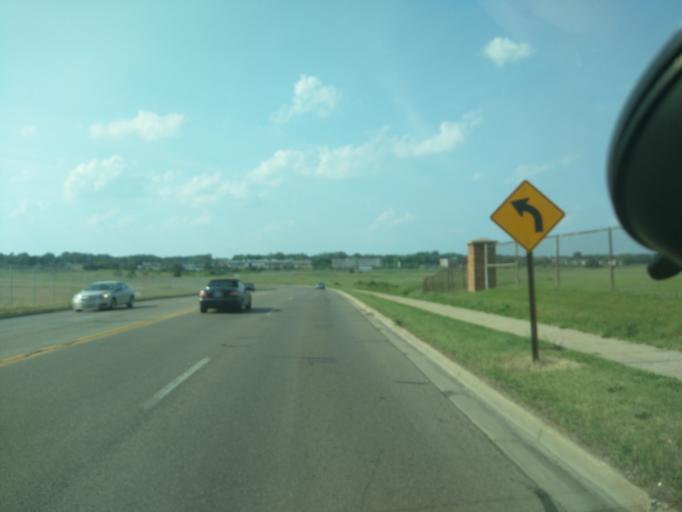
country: US
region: Michigan
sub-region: Jackson County
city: Jackson
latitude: 42.2627
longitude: -84.4484
